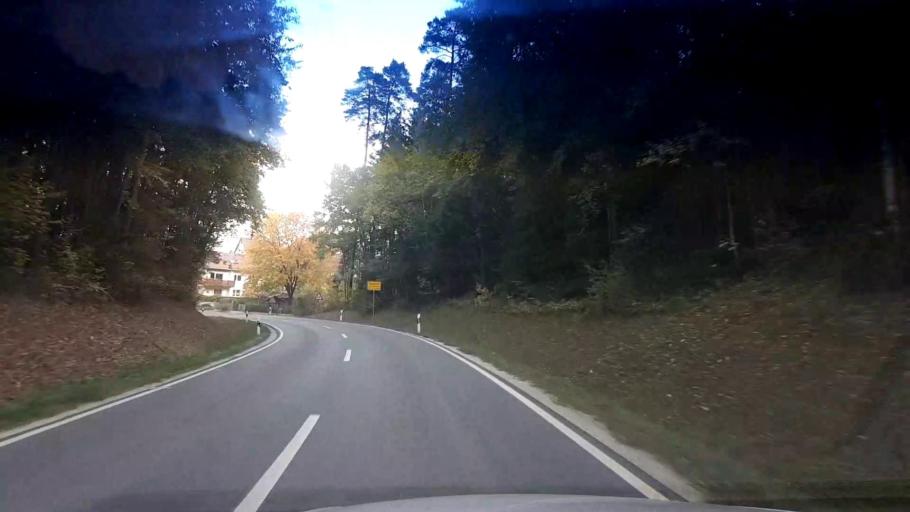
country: DE
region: Bavaria
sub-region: Upper Franconia
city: Altenkunstadt
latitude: 50.1043
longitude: 11.2537
